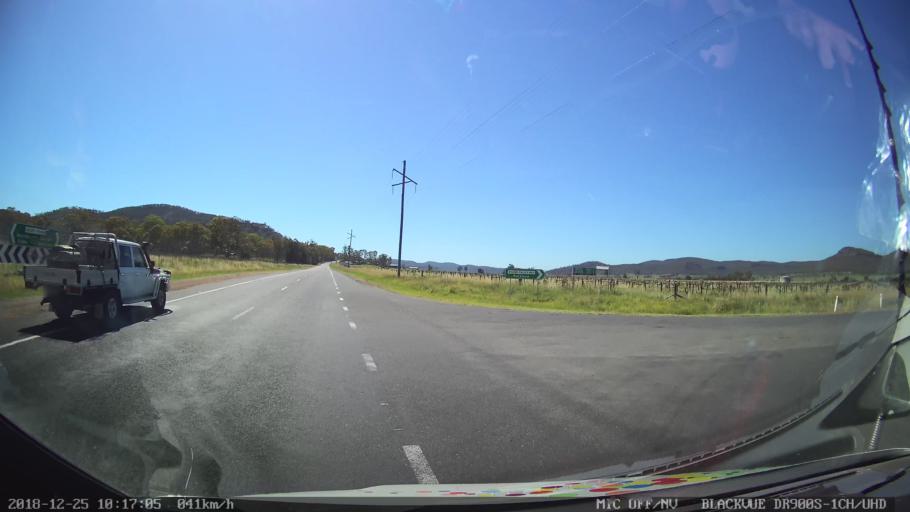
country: AU
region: New South Wales
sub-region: Muswellbrook
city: Denman
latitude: -32.3419
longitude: 150.5807
